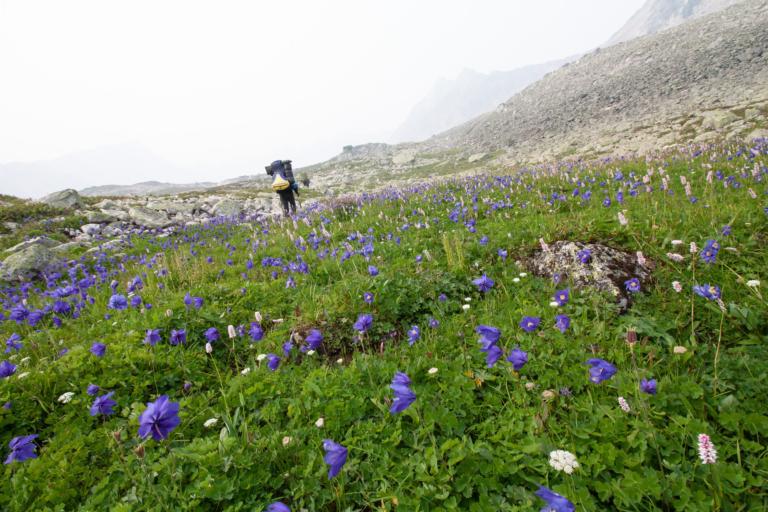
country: RU
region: Respublika Buryatiya
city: Kichera
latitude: 56.2403
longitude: 110.7457
